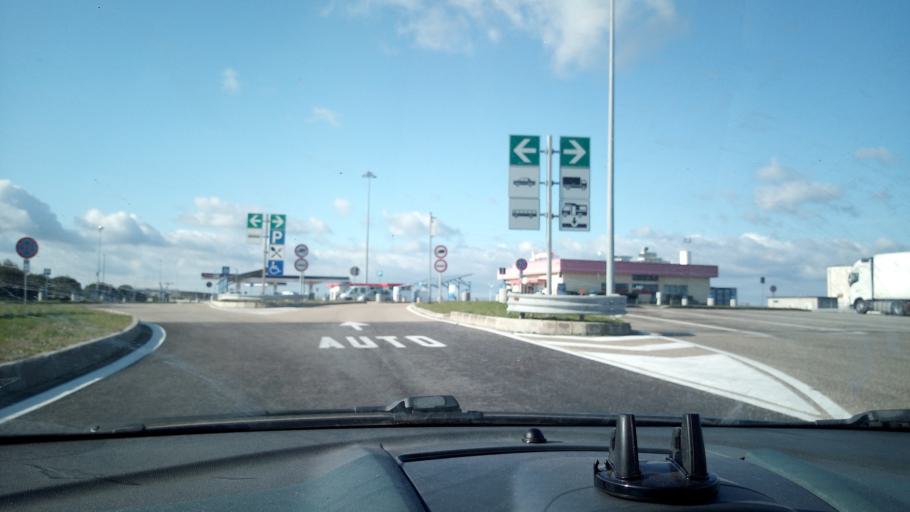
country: IT
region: Apulia
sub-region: Provincia di Foggia
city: Stornara
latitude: 41.1927
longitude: 15.8135
